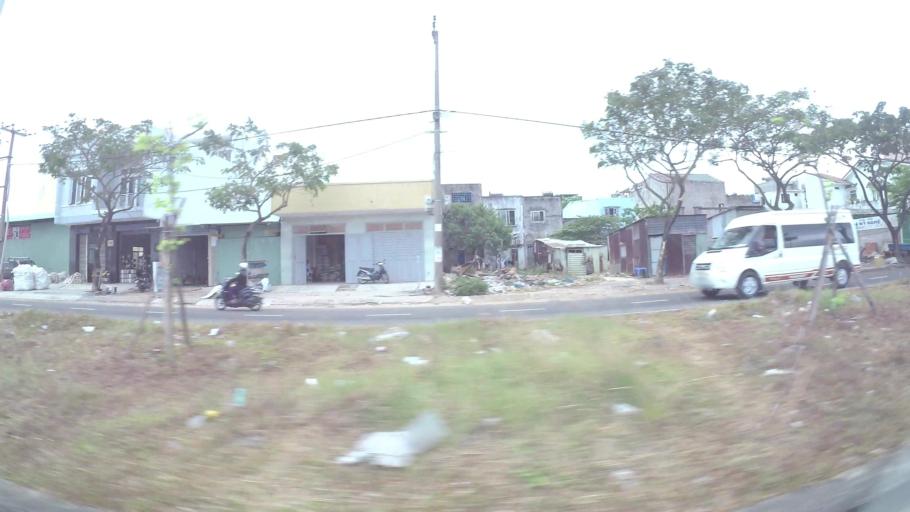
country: VN
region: Da Nang
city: Da Nang
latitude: 16.0939
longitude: 108.2351
